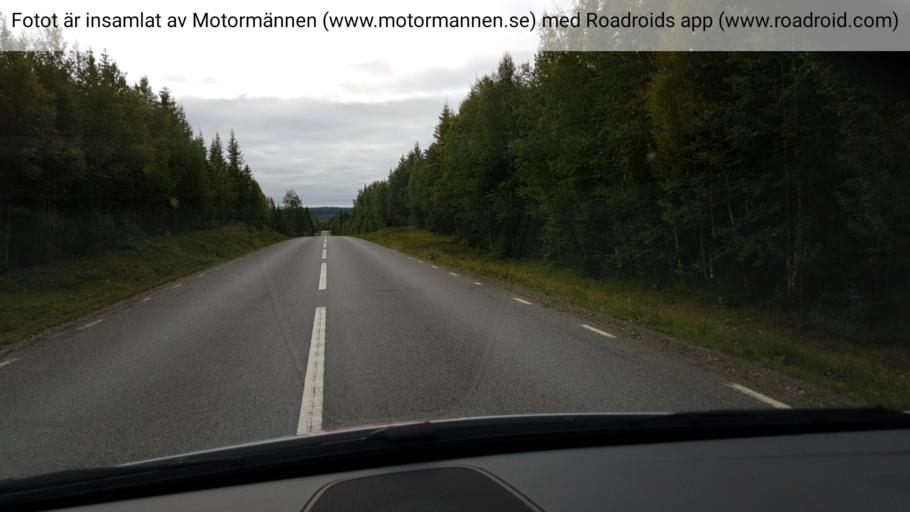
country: NO
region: Nord-Trondelag
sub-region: Lierne
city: Sandvika
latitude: 64.3987
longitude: 14.4941
